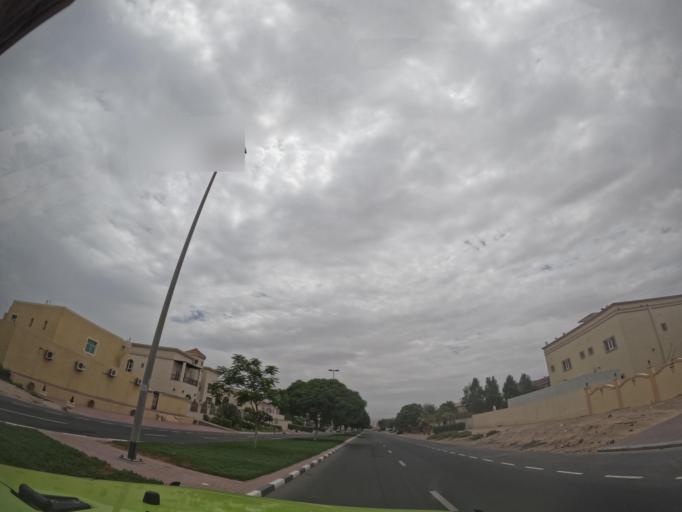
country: AE
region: Ash Shariqah
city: Sharjah
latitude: 25.2009
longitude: 55.3880
